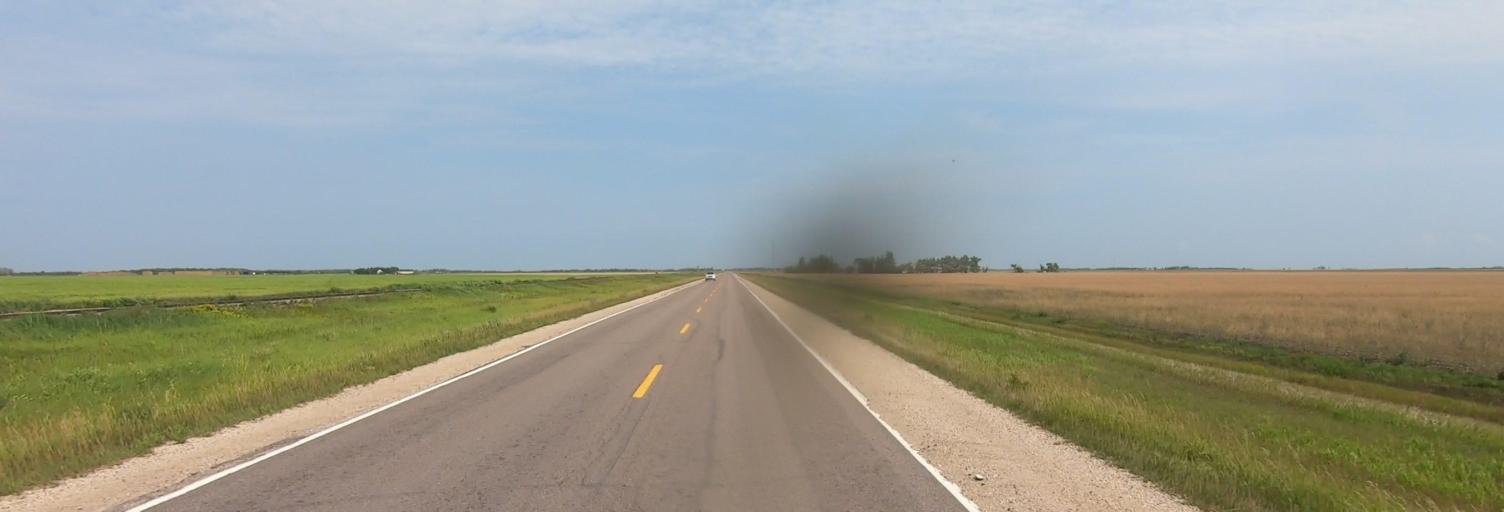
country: CA
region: Manitoba
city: Headingley
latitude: 49.6521
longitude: -97.2937
